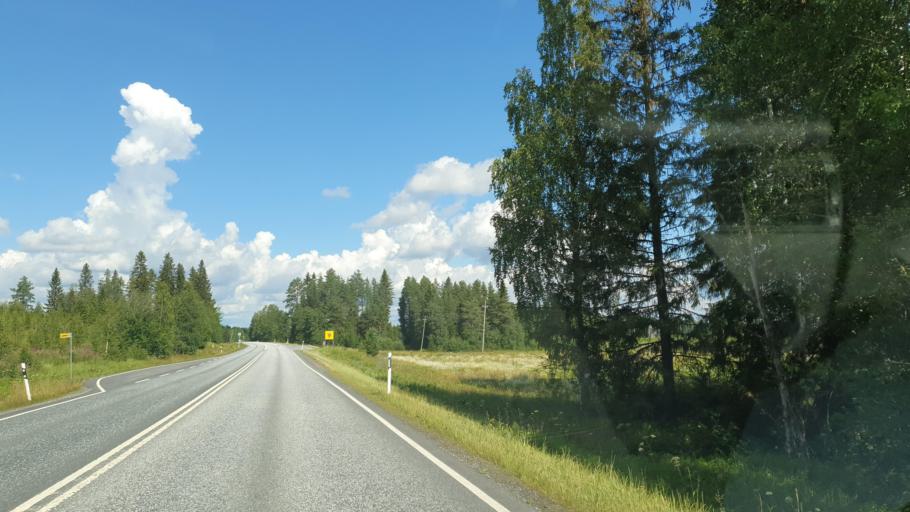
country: FI
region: Northern Savo
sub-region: Ylae-Savo
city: Sonkajaervi
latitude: 63.7950
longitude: 27.4188
